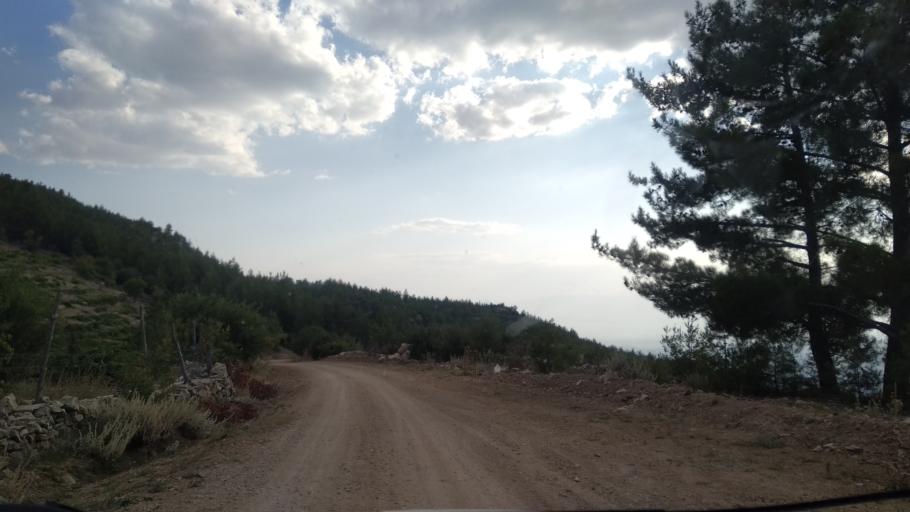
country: TR
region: Mersin
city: Sarikavak
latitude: 36.5899
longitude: 33.6763
